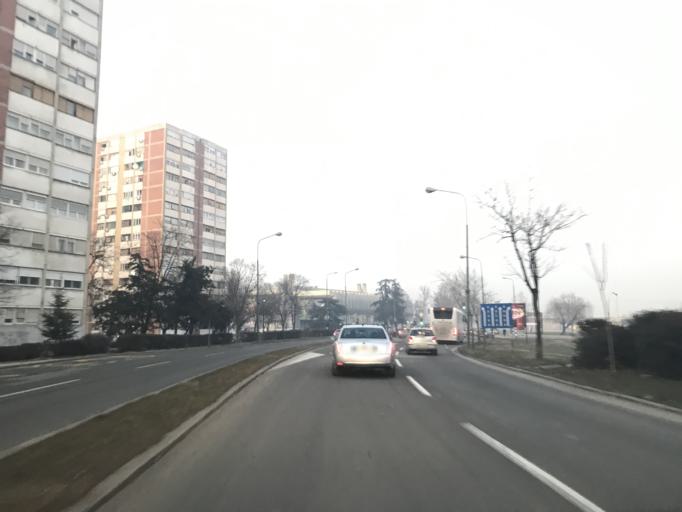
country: RS
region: Central Serbia
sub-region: Sumadijski Okrug
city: Kragujevac
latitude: 44.0117
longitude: 20.9234
